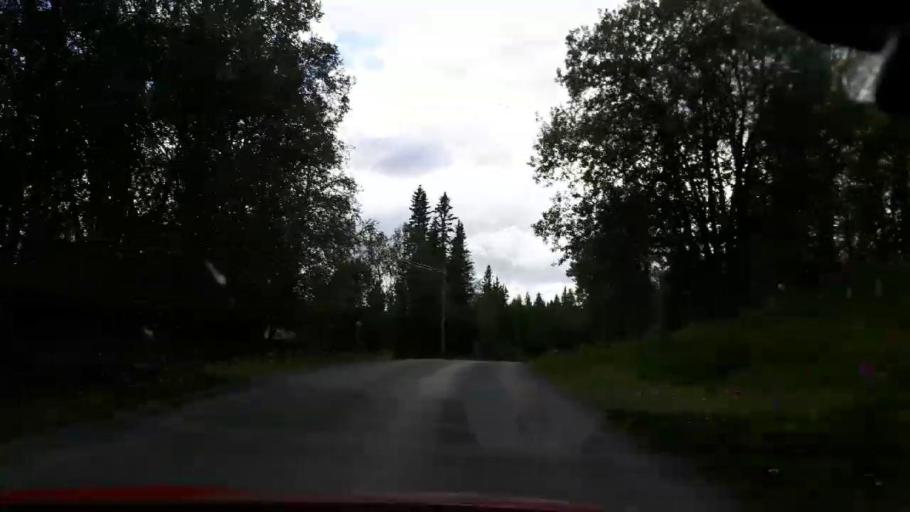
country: SE
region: Jaemtland
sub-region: Are Kommun
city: Are
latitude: 63.1650
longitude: 13.0579
